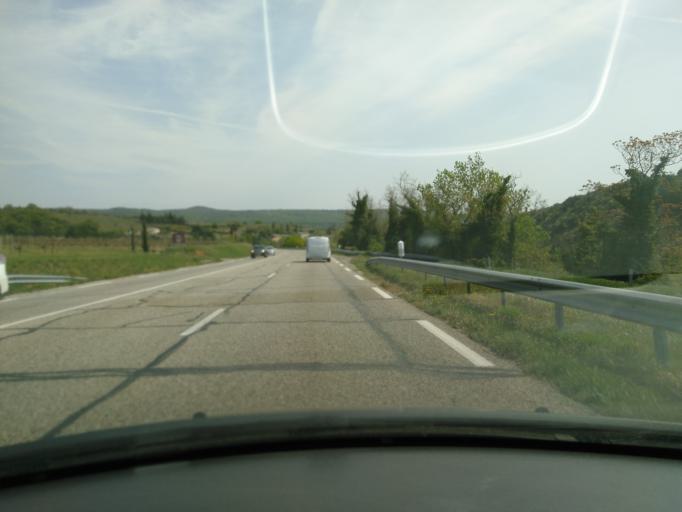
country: FR
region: Rhone-Alpes
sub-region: Departement de l'Ardeche
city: Alba-la-Romaine
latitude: 44.5733
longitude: 4.5813
